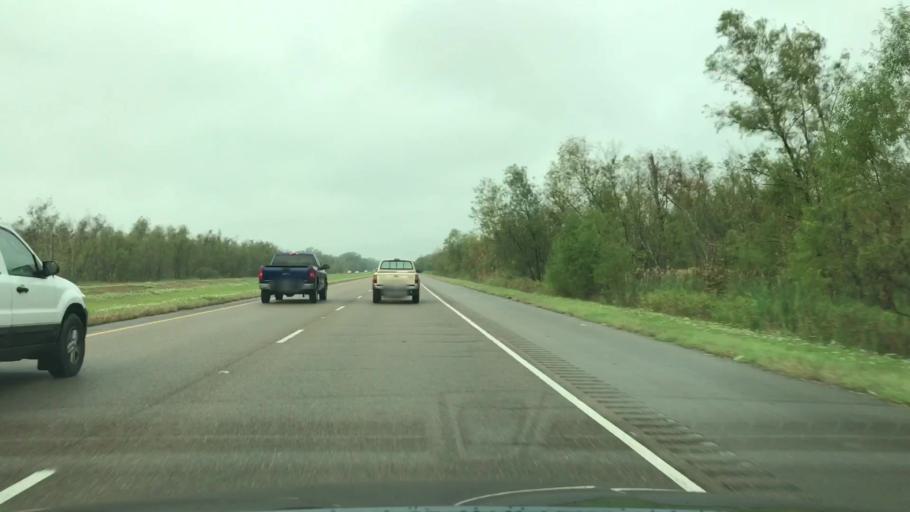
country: US
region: Louisiana
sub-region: Terrebonne Parish
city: Bayou Cane
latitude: 29.6867
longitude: -90.7084
